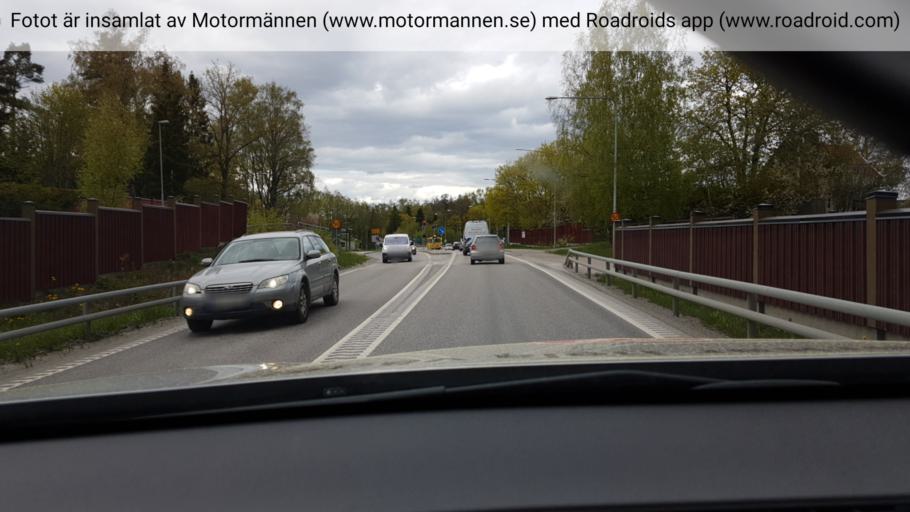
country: SE
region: Stockholm
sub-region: Tyreso Kommun
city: Bollmora
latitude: 59.2088
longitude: 18.2076
